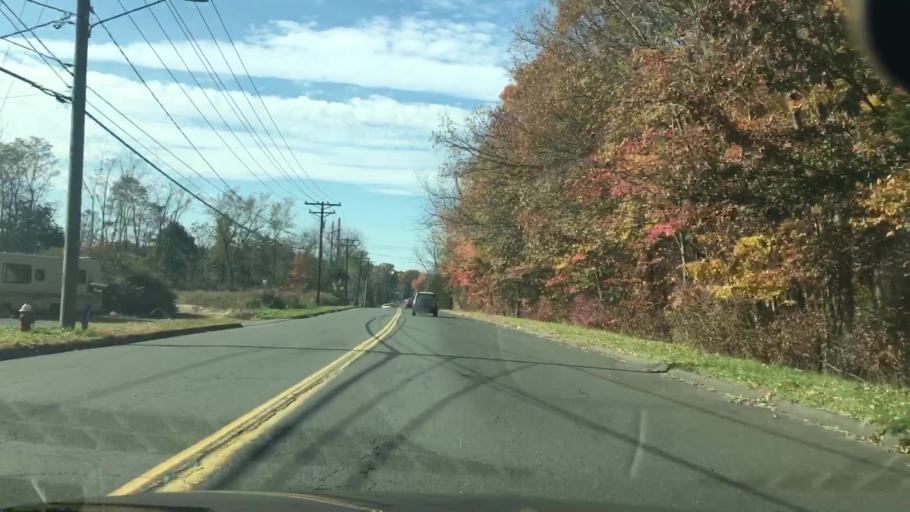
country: US
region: Connecticut
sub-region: Hartford County
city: Kensington
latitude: 41.6404
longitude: -72.7425
